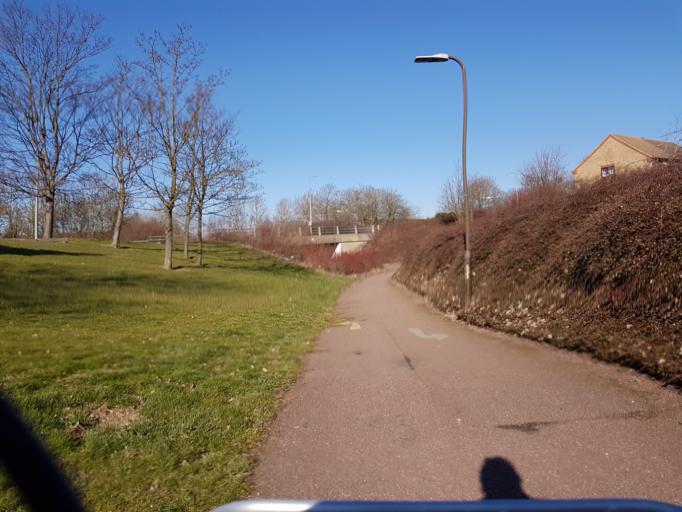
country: GB
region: England
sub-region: Milton Keynes
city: Milton Keynes
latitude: 52.0255
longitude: -0.7572
